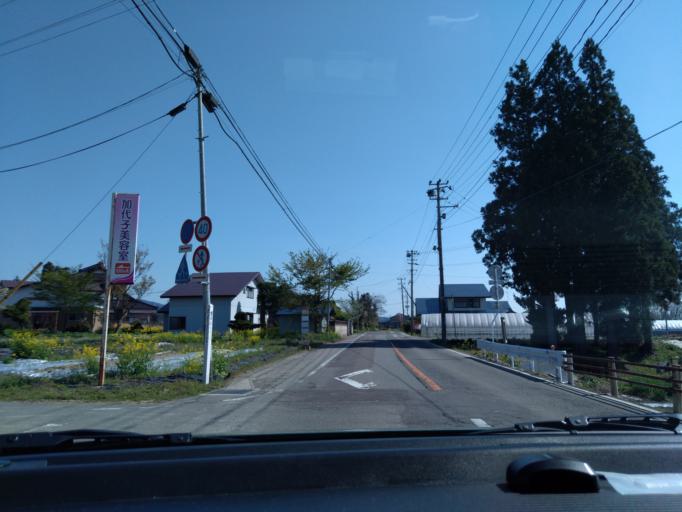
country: JP
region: Akita
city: Kakunodatemachi
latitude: 39.4941
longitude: 140.5941
